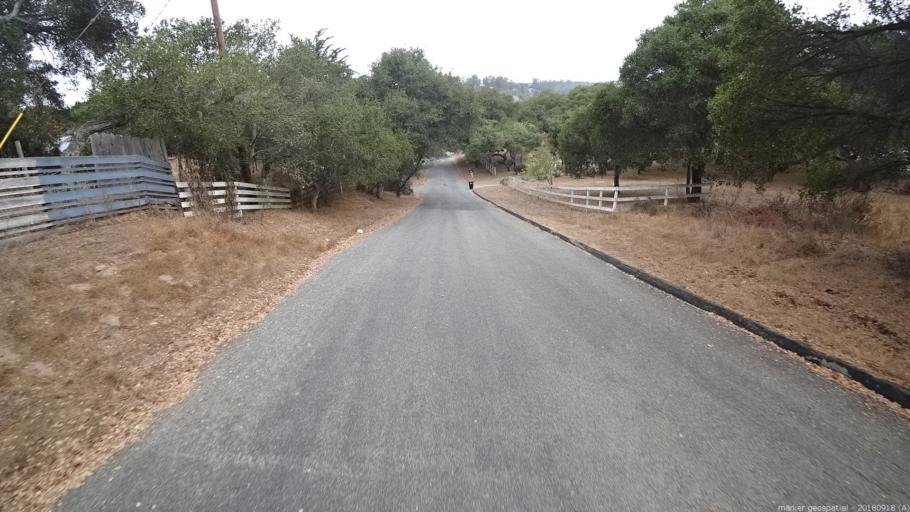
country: US
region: California
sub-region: Monterey County
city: Prunedale
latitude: 36.7795
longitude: -121.6331
